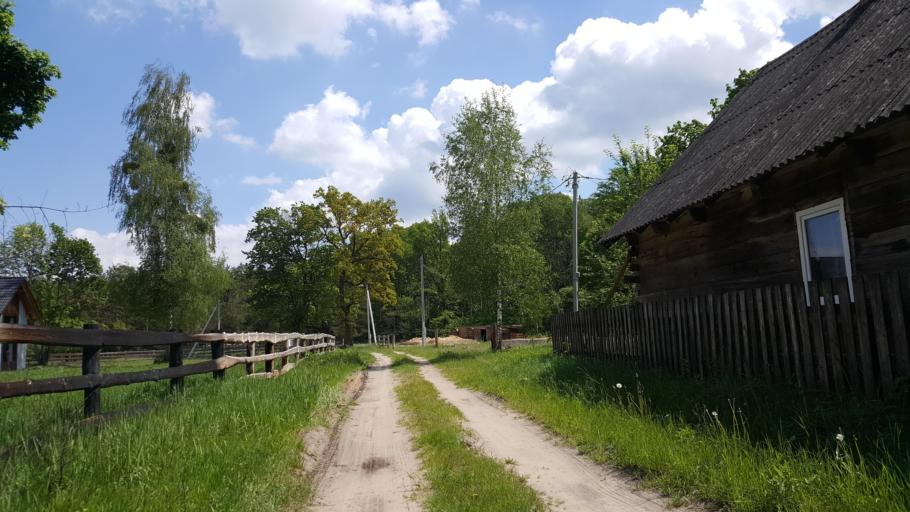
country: BY
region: Brest
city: Kamyanyuki
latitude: 52.4950
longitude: 23.9595
